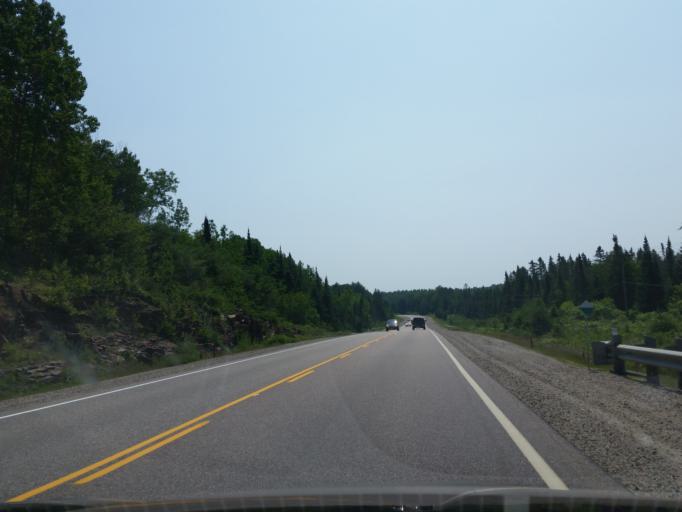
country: CA
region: Ontario
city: Deep River
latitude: 46.1774
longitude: -77.7186
